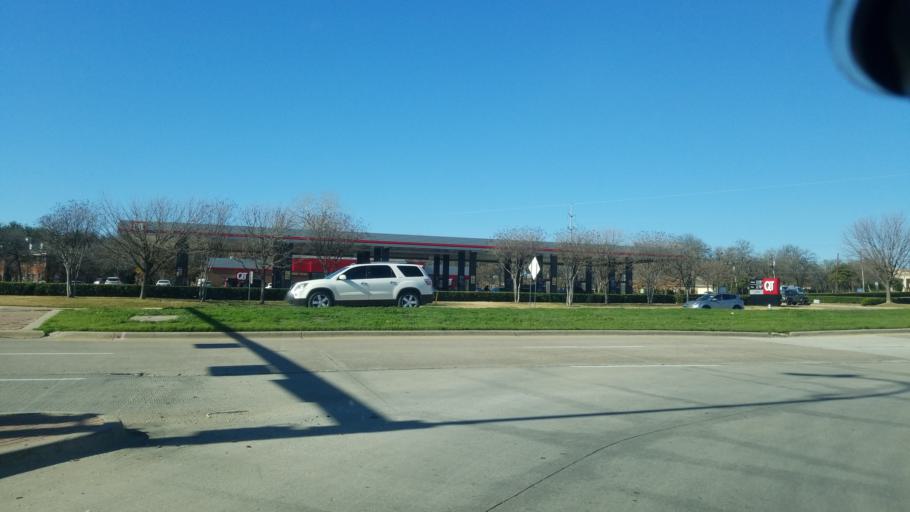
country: US
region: Texas
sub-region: Tarrant County
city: Arlington
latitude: 32.7628
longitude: -97.0751
